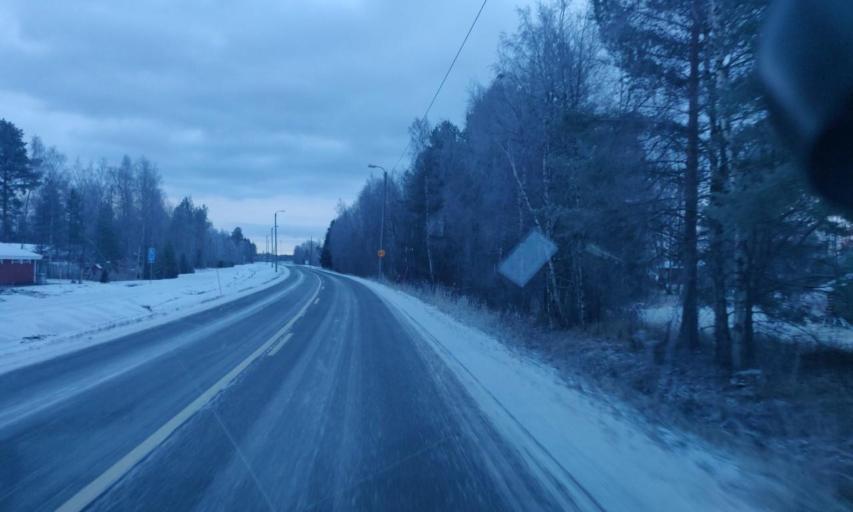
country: FI
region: Northern Ostrobothnia
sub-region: Oulu
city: Oulunsalo
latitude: 64.9872
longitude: 25.2599
